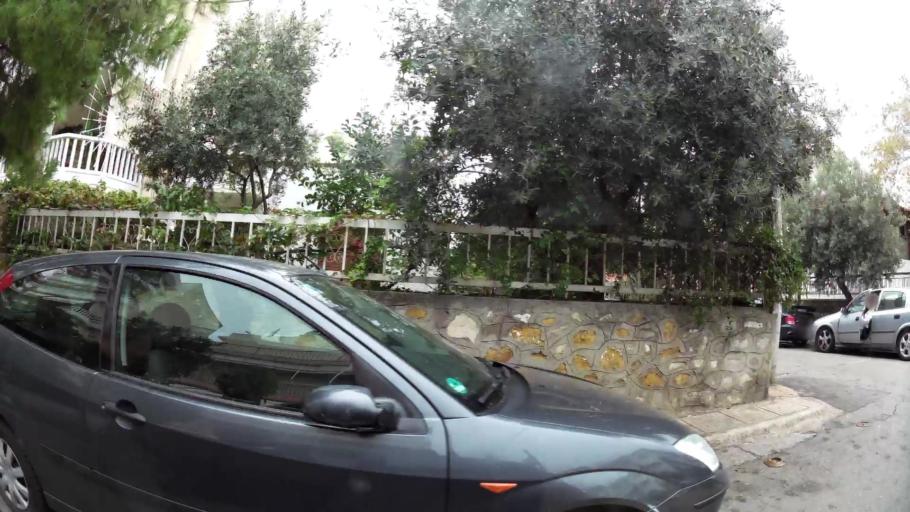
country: GR
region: Attica
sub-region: Nomarchia Athinas
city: Chaidari
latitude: 38.0072
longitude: 23.6661
